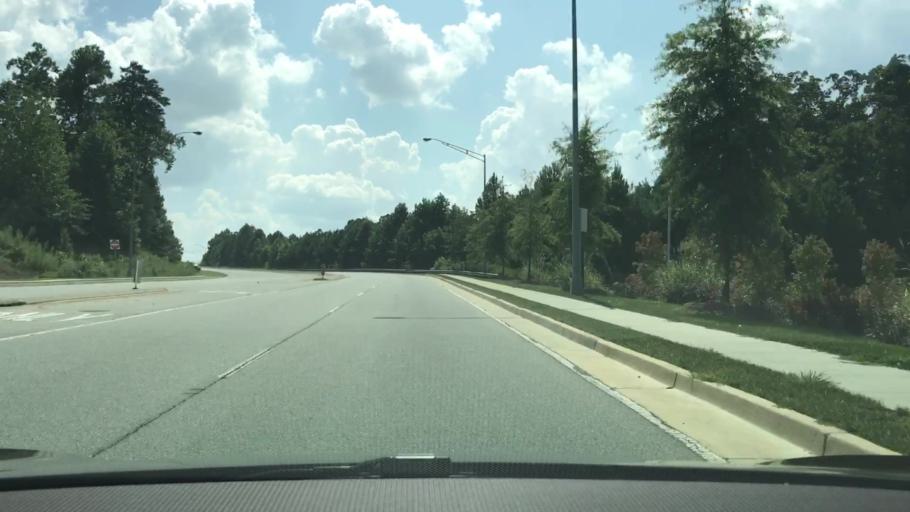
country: US
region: Georgia
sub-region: Gwinnett County
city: Buford
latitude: 34.0862
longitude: -84.0001
